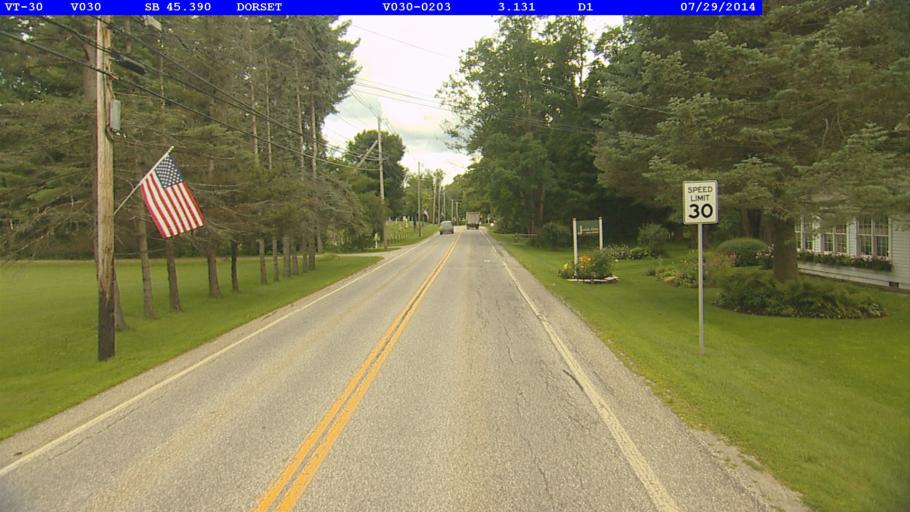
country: US
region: Vermont
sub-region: Bennington County
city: Manchester Center
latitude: 43.2522
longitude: -73.0957
